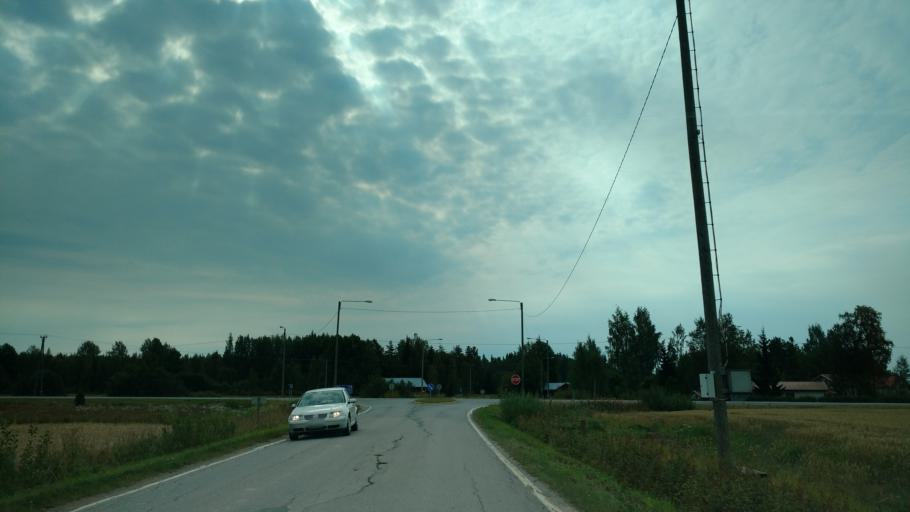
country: FI
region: Varsinais-Suomi
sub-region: Loimaa
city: Koski Tl
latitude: 60.7054
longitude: 23.1656
